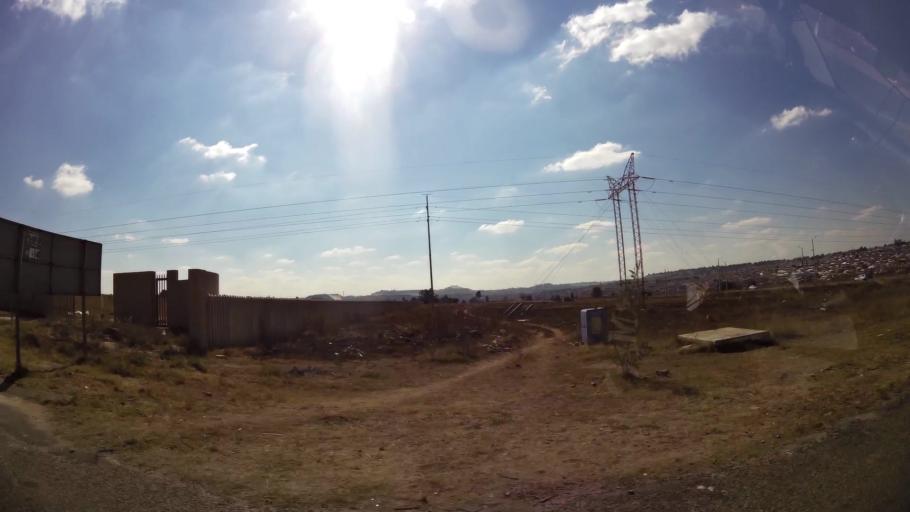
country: ZA
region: Gauteng
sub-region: West Rand District Municipality
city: Randfontein
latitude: -26.1634
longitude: 27.7605
